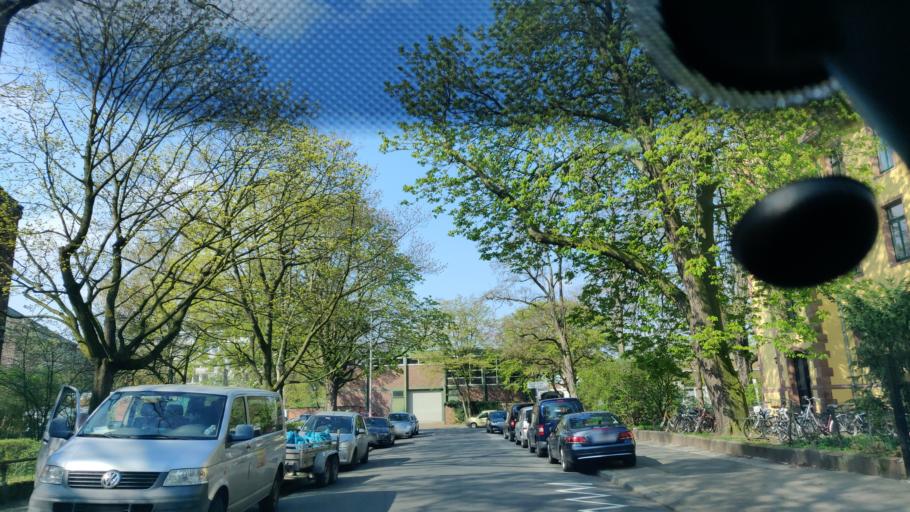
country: DE
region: Lower Saxony
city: Hannover
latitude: 52.3685
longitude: 9.7683
